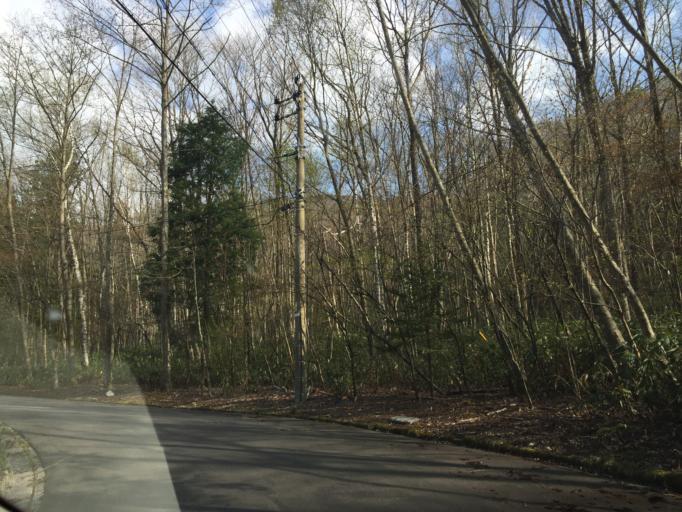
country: JP
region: Nagano
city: Iida
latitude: 35.3522
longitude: 137.6783
